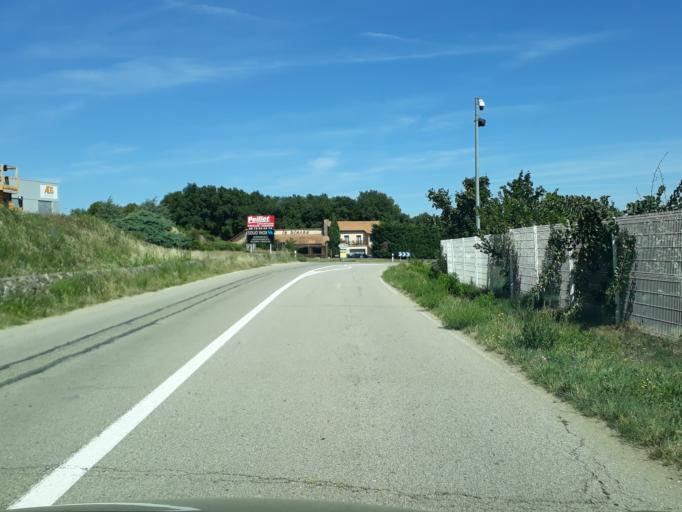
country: FR
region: Rhone-Alpes
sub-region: Departement de l'Ardeche
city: Felines
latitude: 45.3042
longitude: 4.7341
